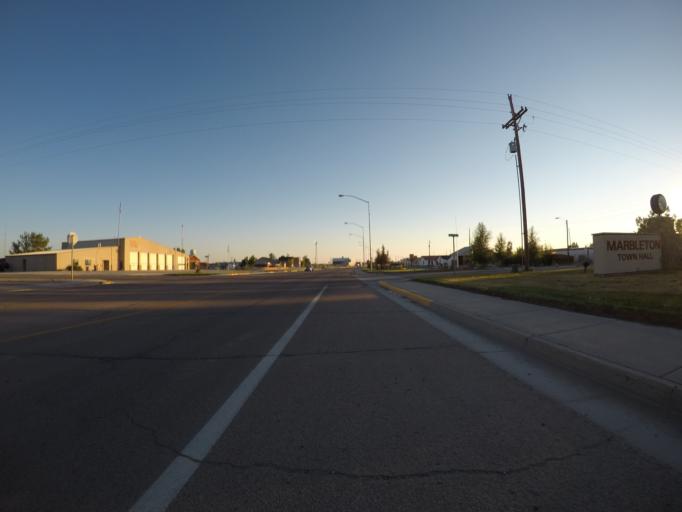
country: US
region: Wyoming
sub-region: Sublette County
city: Marbleton
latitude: 42.5542
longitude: -110.1095
